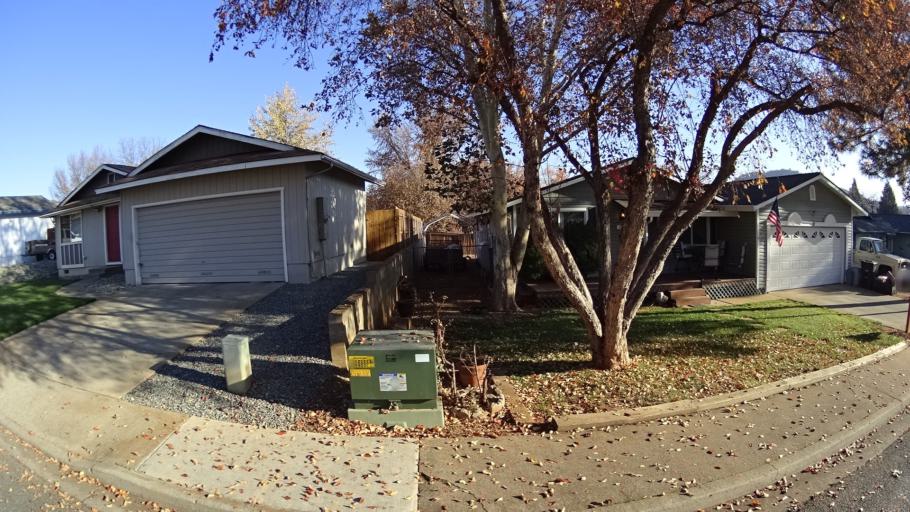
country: US
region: California
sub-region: Siskiyou County
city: Yreka
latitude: 41.7213
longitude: -122.6465
